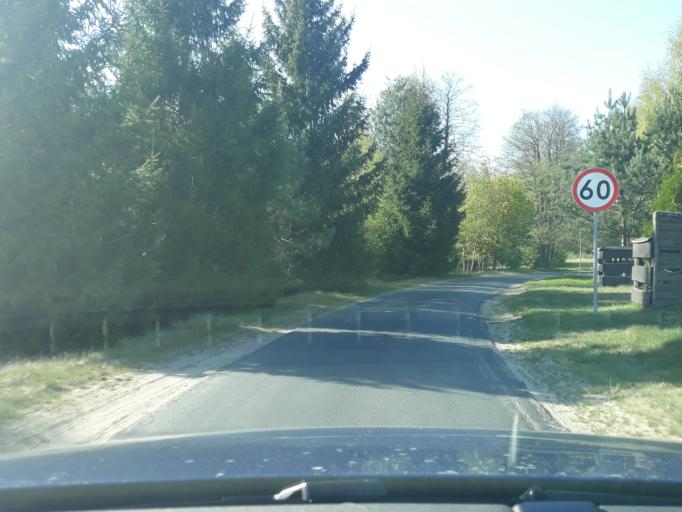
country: PL
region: Pomeranian Voivodeship
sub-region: Powiat czluchowski
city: Przechlewo
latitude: 53.8785
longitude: 17.3230
